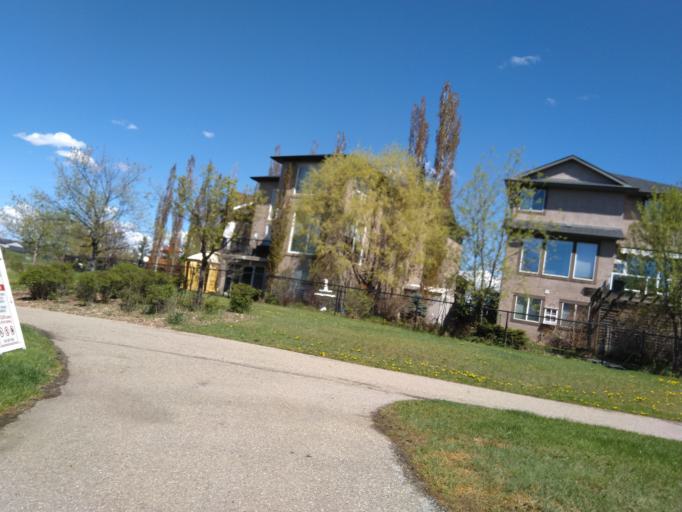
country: CA
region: Alberta
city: Chestermere
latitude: 51.0207
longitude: -113.8324
